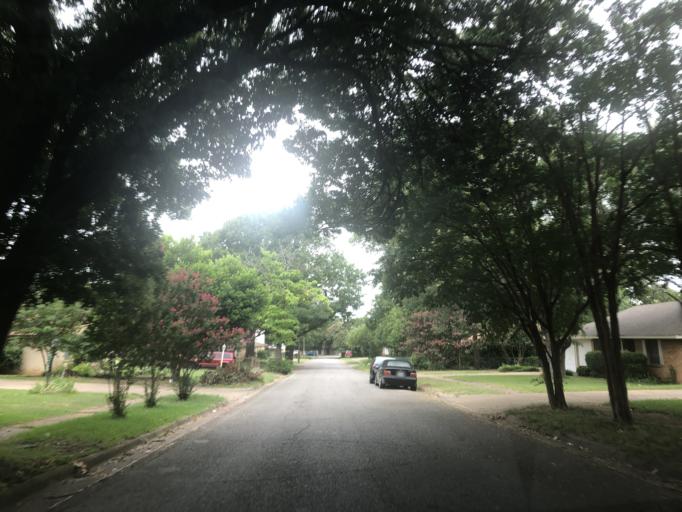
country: US
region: Texas
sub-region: Dallas County
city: Duncanville
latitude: 32.6545
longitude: -96.9145
